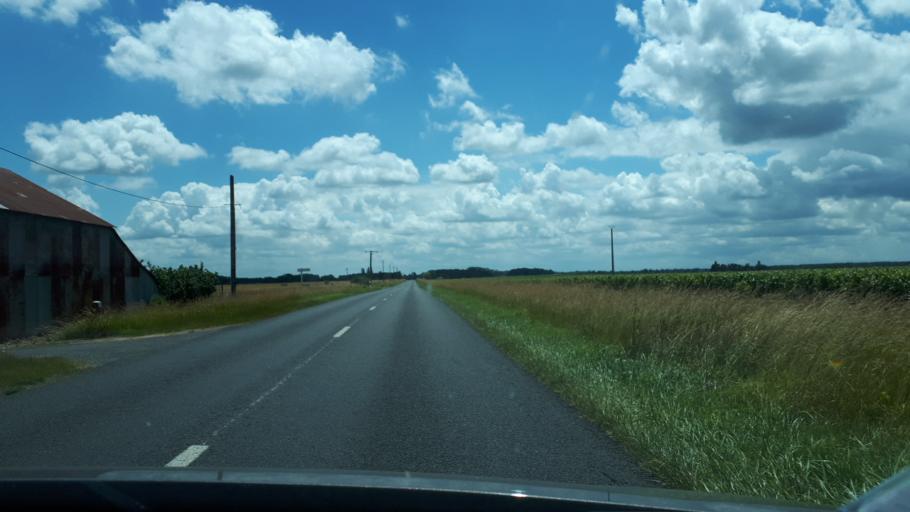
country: FR
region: Centre
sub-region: Departement du Loir-et-Cher
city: Contres
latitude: 47.3830
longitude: 1.4073
